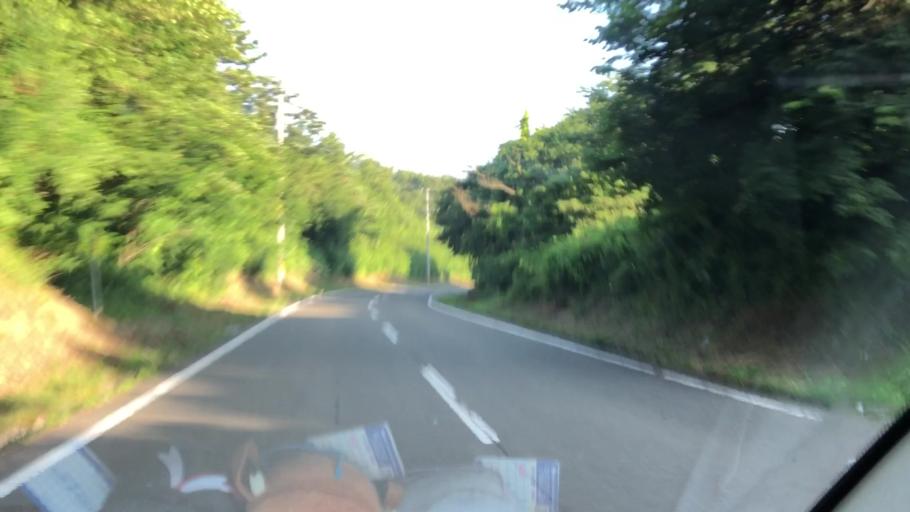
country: JP
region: Miyagi
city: Shiroishi
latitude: 38.0361
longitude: 140.5364
